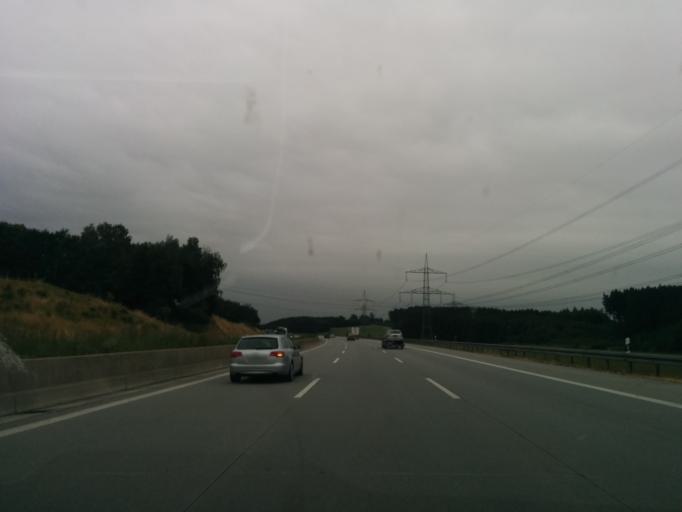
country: DE
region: Bavaria
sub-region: Swabia
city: Dasing
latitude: 48.3974
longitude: 11.0238
